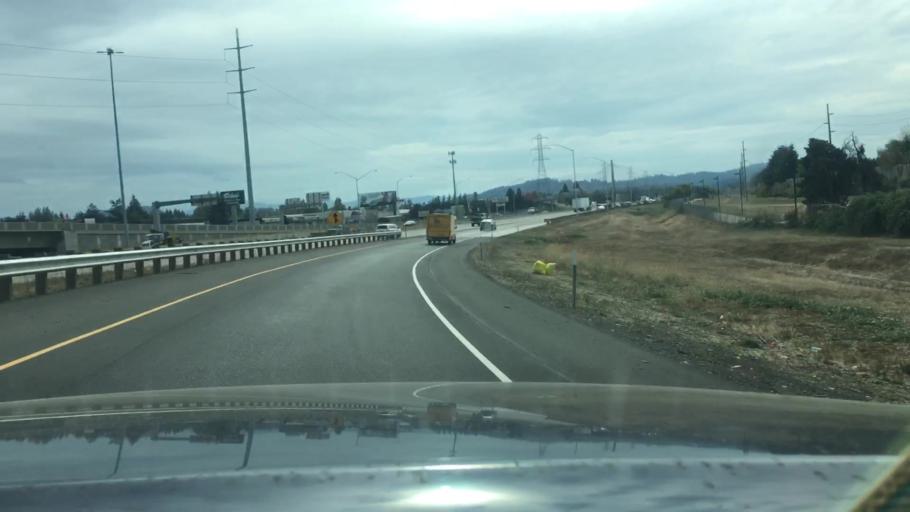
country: US
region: Oregon
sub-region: Lane County
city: Springfield
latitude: 44.0819
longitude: -123.0480
